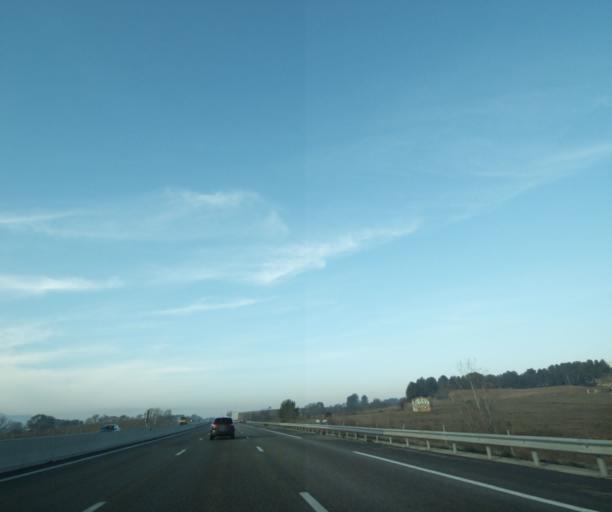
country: FR
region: Provence-Alpes-Cote d'Azur
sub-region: Departement des Bouches-du-Rhone
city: Trets
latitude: 43.4707
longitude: 5.6703
